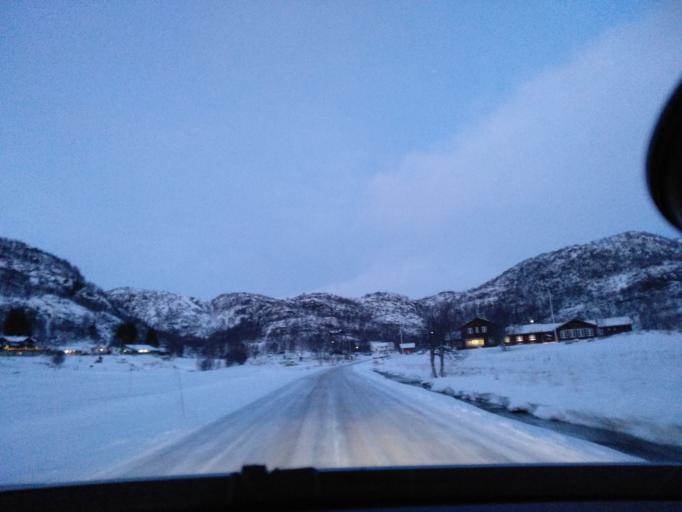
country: NO
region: Vest-Agder
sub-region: Sirdal
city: Tonstad
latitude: 59.0210
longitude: 6.9239
